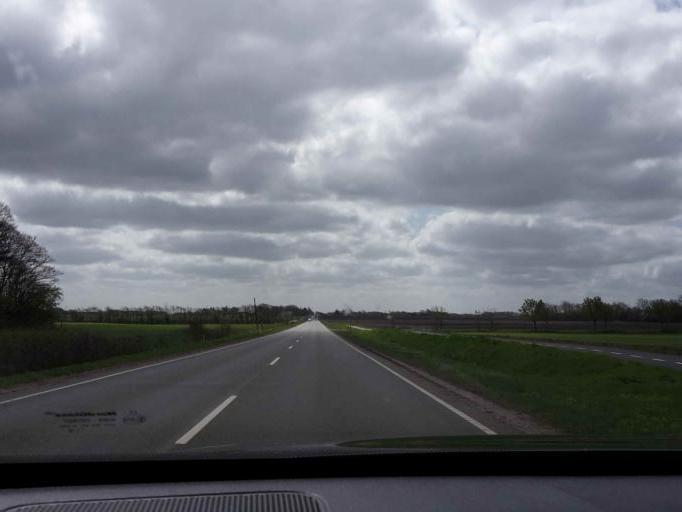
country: DK
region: South Denmark
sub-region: Varde Kommune
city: Olgod
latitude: 55.7594
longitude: 8.6201
